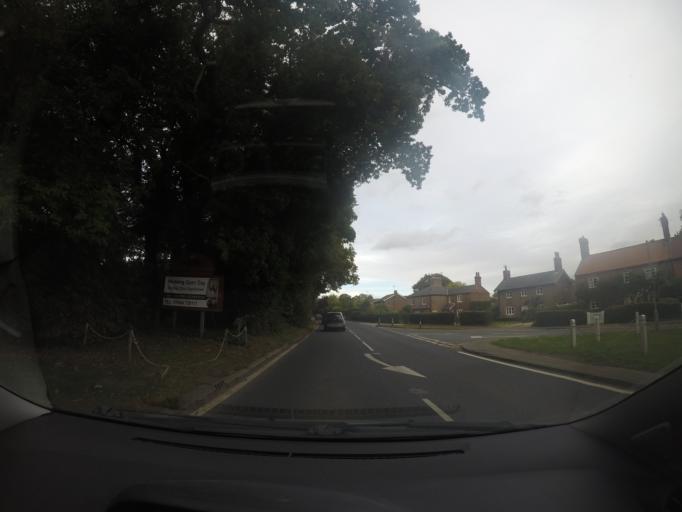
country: GB
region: England
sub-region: City of York
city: Deighton
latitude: 53.8784
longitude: -1.0448
